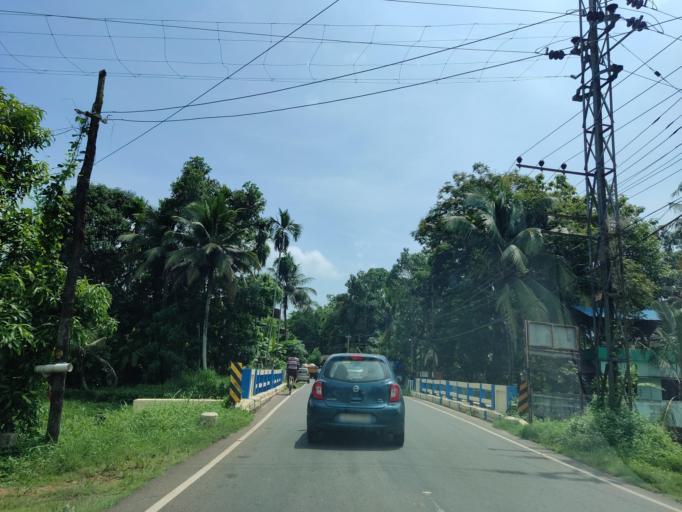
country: IN
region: Kerala
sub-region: Alappuzha
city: Chengannur
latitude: 9.3077
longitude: 76.5896
